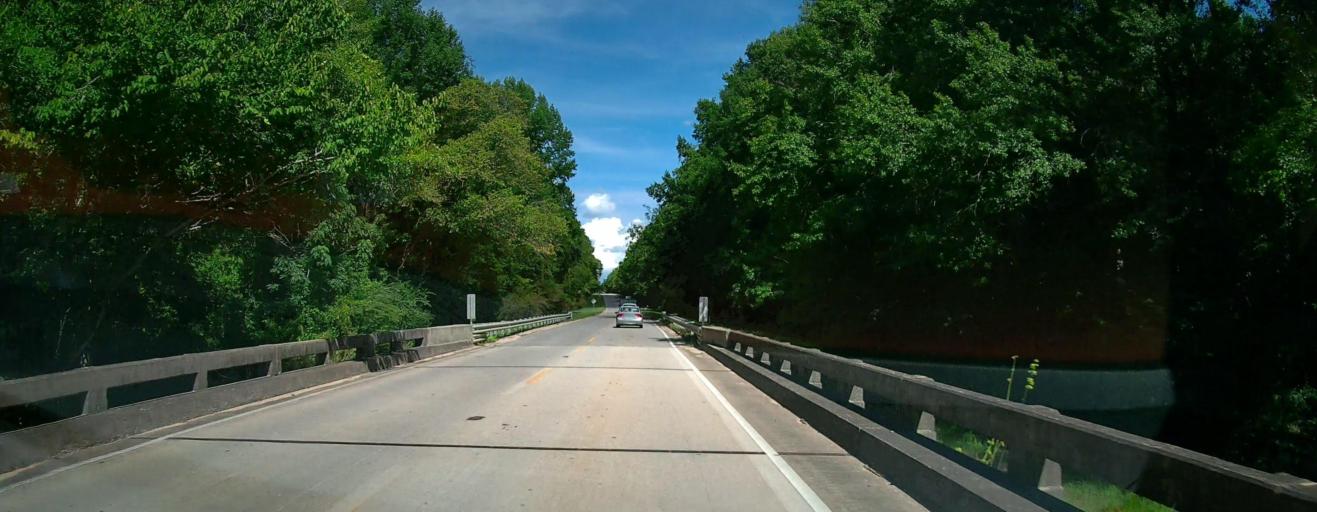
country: US
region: Alabama
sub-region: Macon County
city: Tuskegee
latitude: 32.3796
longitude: -85.7947
